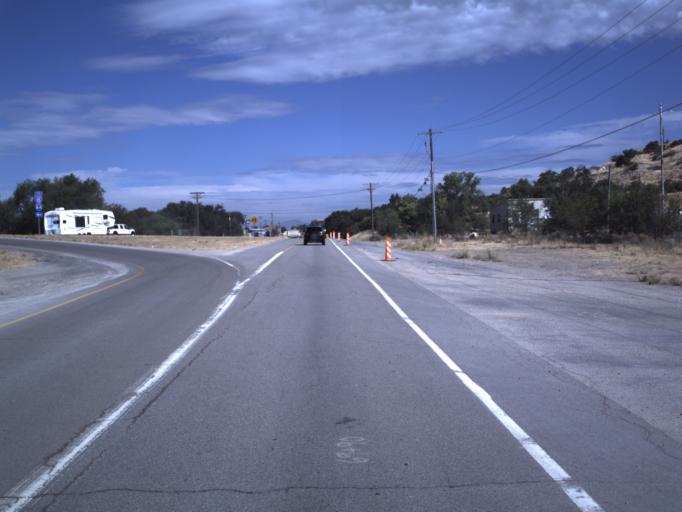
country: US
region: Utah
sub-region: Box Elder County
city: South Willard
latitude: 41.3447
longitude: -112.0326
